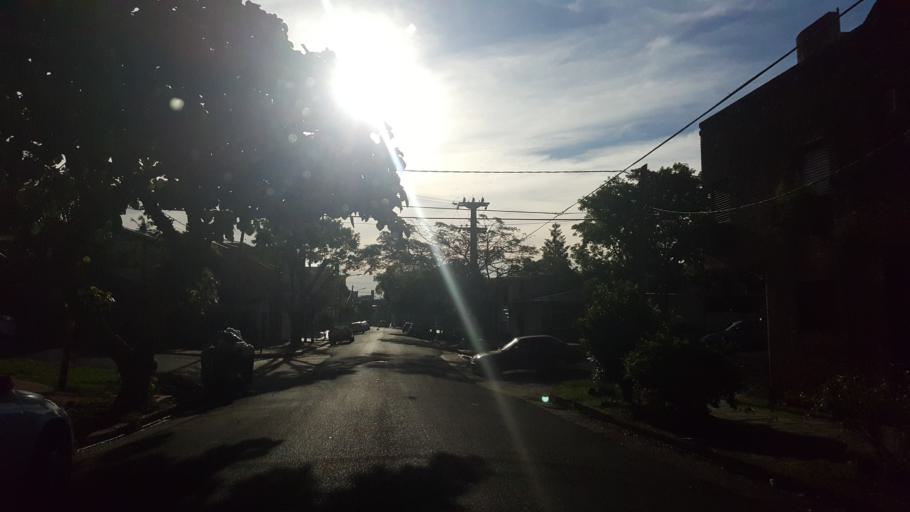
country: AR
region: Misiones
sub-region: Departamento de Capital
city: Posadas
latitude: -27.3596
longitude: -55.8986
